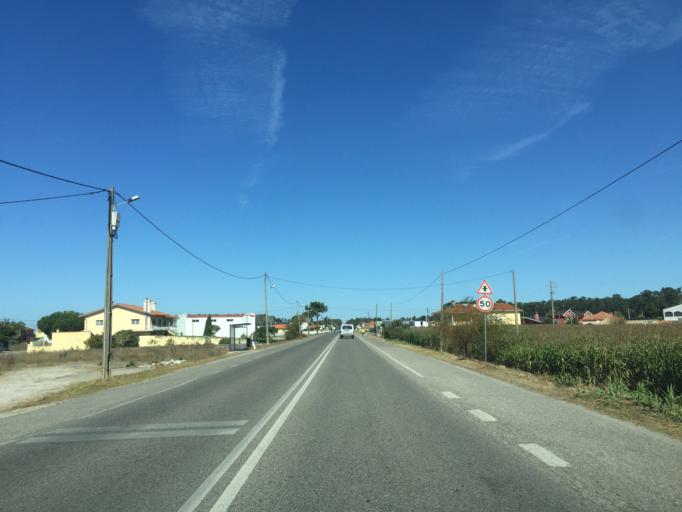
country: PT
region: Coimbra
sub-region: Figueira da Foz
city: Alhadas
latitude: 40.2670
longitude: -8.7790
